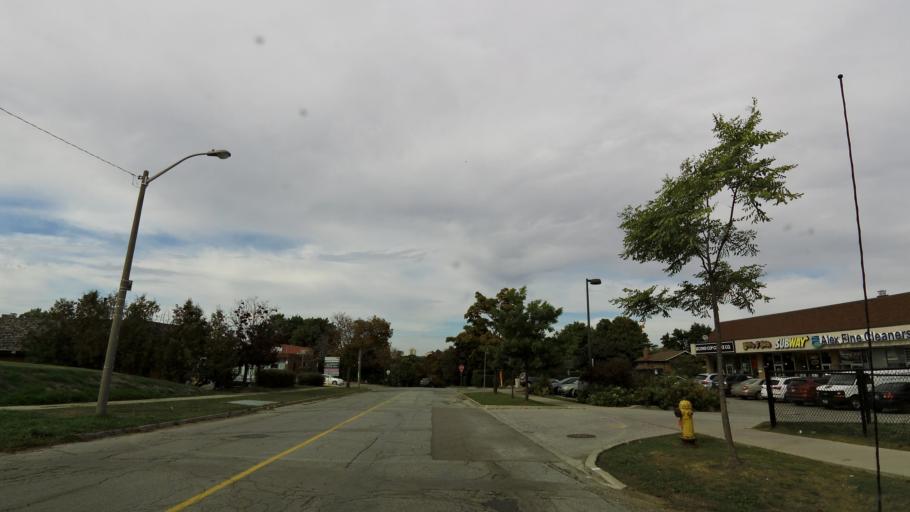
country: CA
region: Ontario
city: Etobicoke
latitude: 43.6790
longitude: -79.5451
